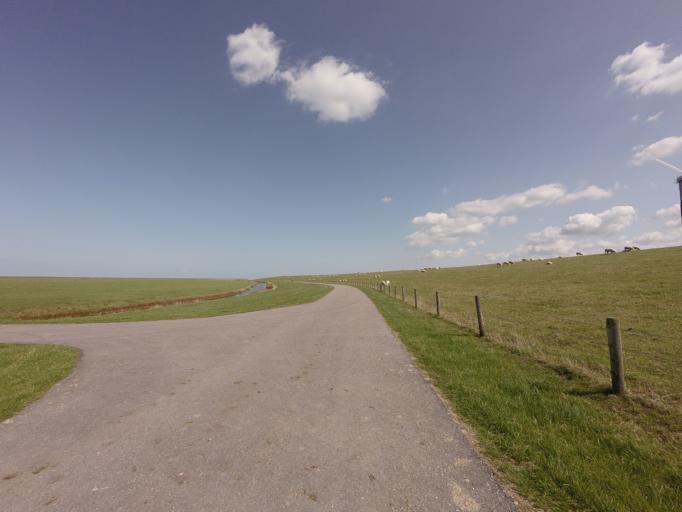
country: NL
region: Friesland
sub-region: Gemeente Ferwerderadiel
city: Marrum
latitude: 53.3339
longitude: 5.7796
